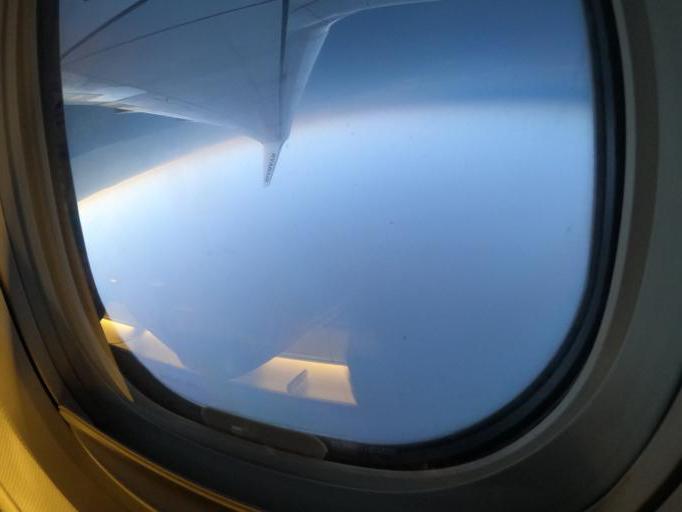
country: FR
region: Nord-Pas-de-Calais
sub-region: Departement du Nord
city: Ghyvelde
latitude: 51.0369
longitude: 2.5764
